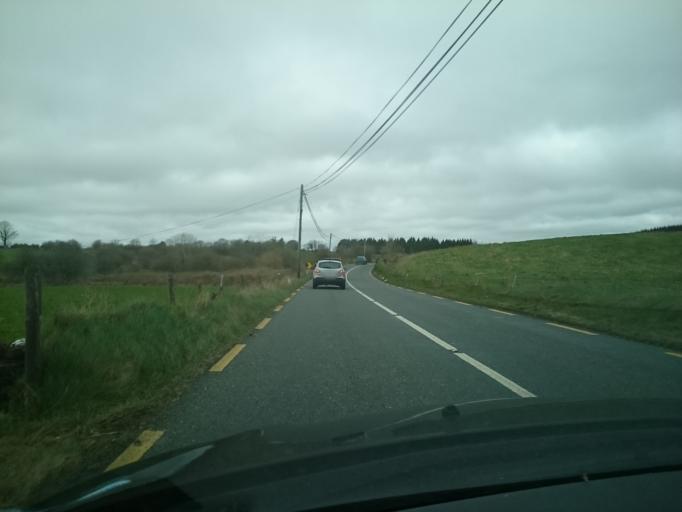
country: IE
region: Connaught
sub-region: Maigh Eo
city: Kiltamagh
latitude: 53.7902
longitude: -9.0891
